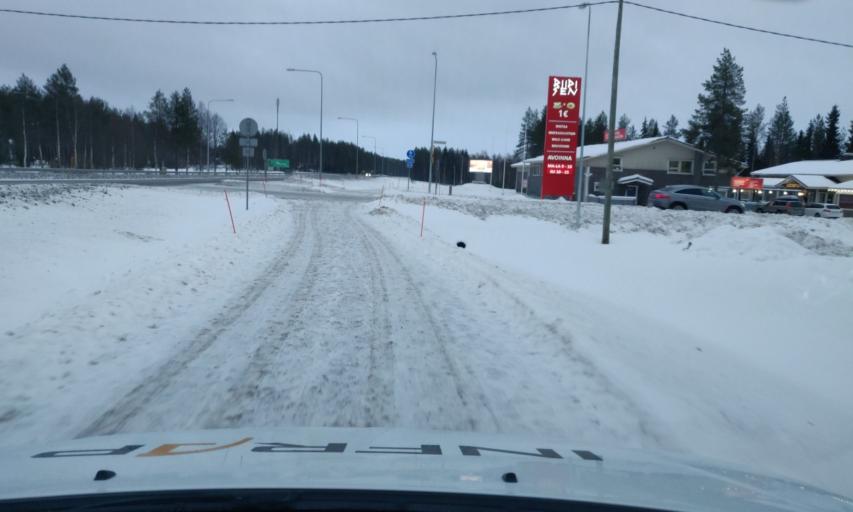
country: FI
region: Northern Ostrobothnia
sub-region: Koillismaa
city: Kuusamo
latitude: 65.9901
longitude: 29.1559
